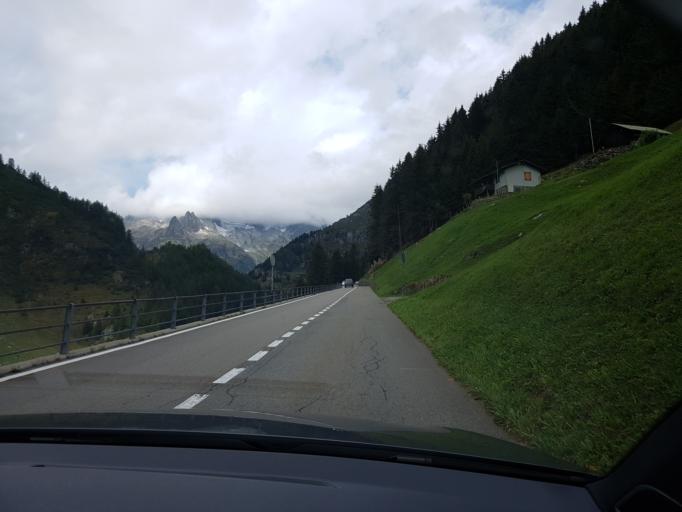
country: CH
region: Uri
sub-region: Uri
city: Andermatt
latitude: 46.7368
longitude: 8.5199
